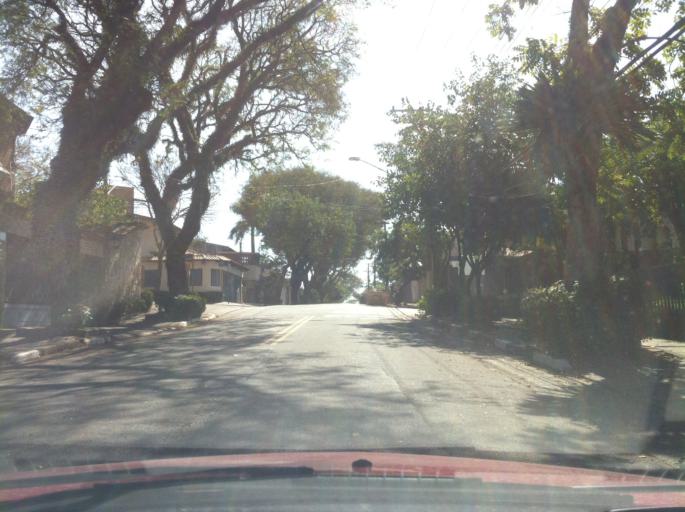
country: BR
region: Sao Paulo
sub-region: Diadema
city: Diadema
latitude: -23.6241
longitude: -46.6434
